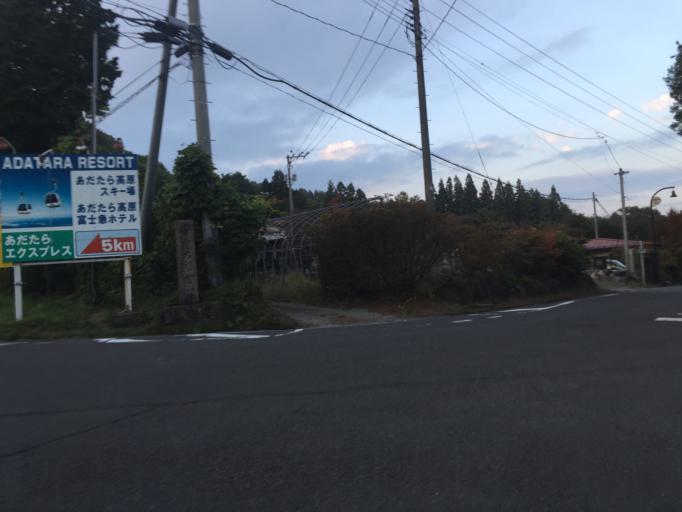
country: JP
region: Fukushima
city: Nihommatsu
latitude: 37.6074
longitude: 140.3547
